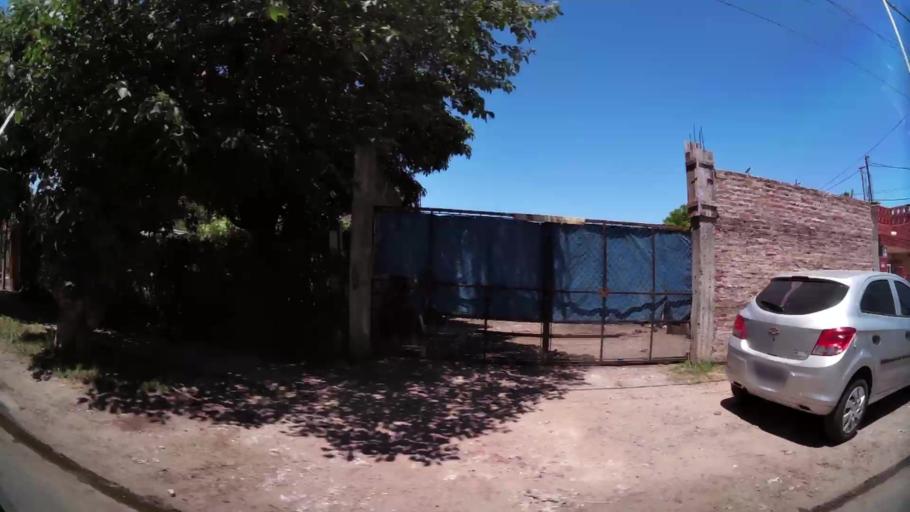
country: AR
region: Buenos Aires
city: Hurlingham
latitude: -34.5123
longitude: -58.7086
